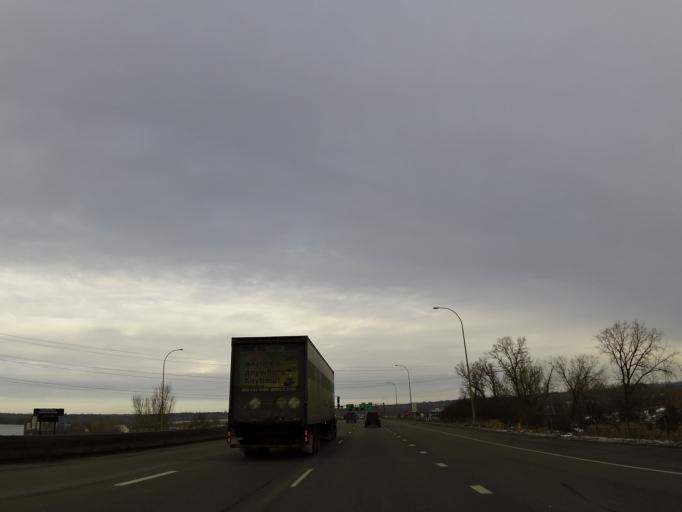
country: US
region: Minnesota
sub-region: Dakota County
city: Burnsville
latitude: 44.7797
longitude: -93.2883
